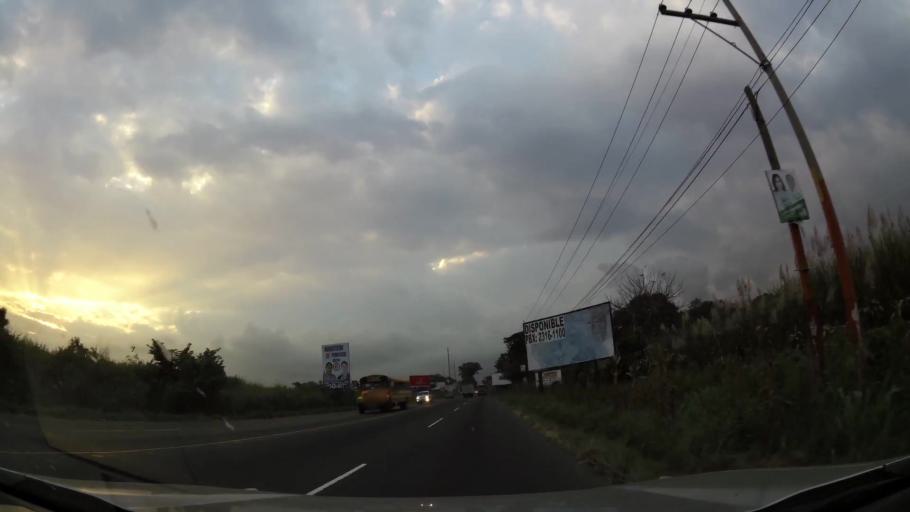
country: GT
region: Escuintla
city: Siquinala
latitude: 14.2945
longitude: -90.9448
